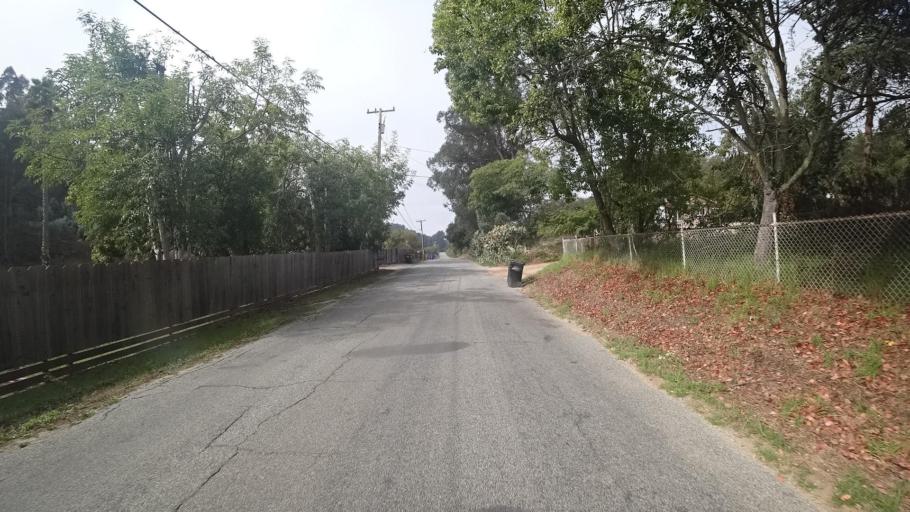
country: US
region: California
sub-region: Monterey County
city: Las Lomas
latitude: 36.8827
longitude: -121.7132
